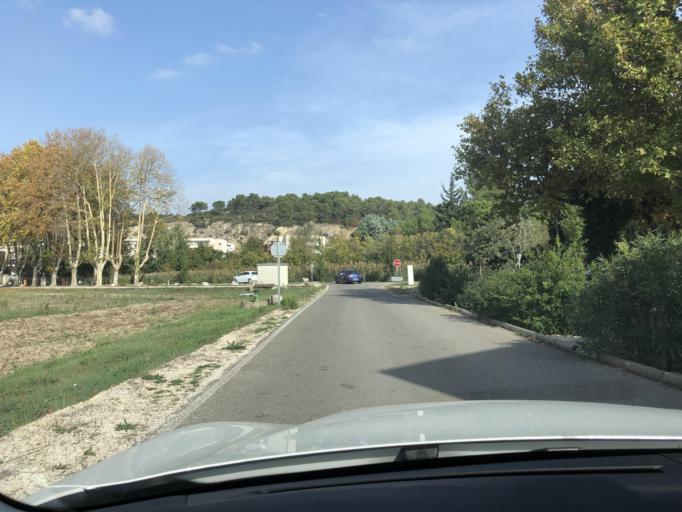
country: FR
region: Provence-Alpes-Cote d'Azur
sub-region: Departement du Vaucluse
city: Montfavet
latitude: 43.9163
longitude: 4.8795
